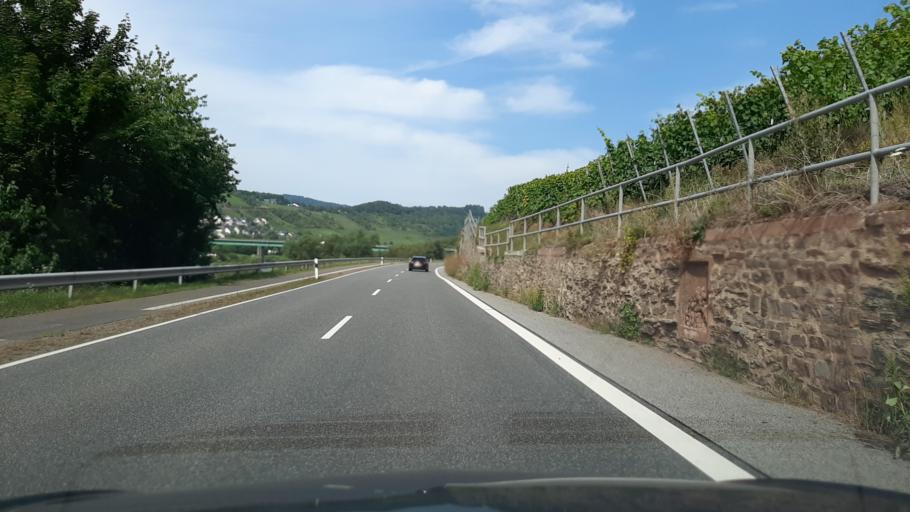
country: DE
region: Rheinland-Pfalz
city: Reil
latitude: 50.0198
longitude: 7.1220
